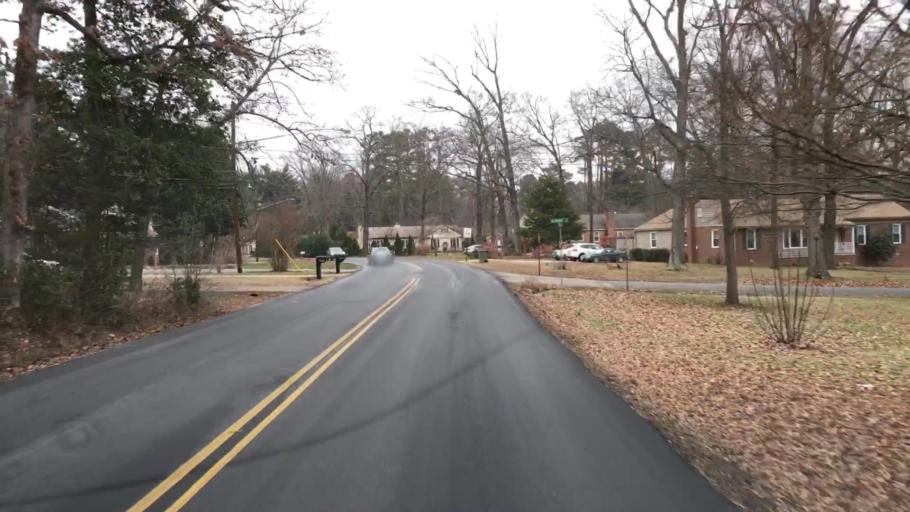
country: US
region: Virginia
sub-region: Chesterfield County
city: Bon Air
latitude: 37.5404
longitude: -77.5724
